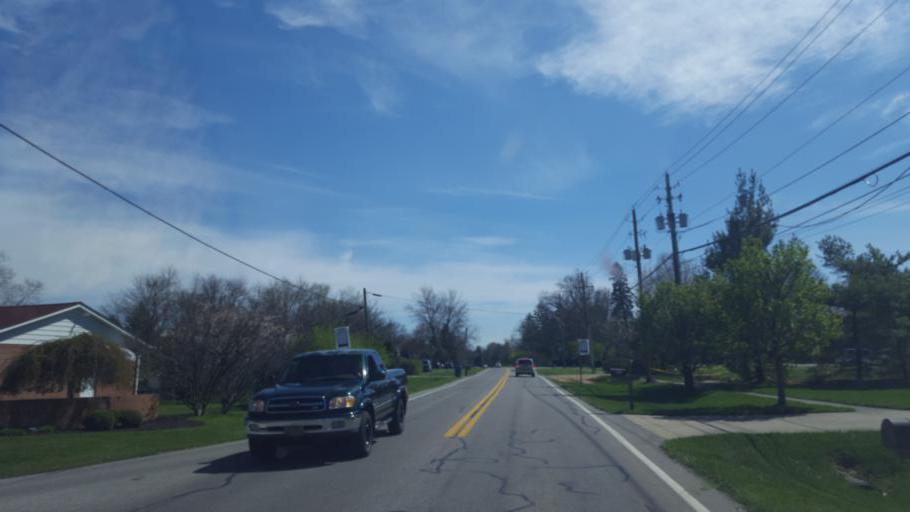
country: US
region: Ohio
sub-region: Franklin County
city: Worthington
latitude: 40.0837
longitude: -83.0498
